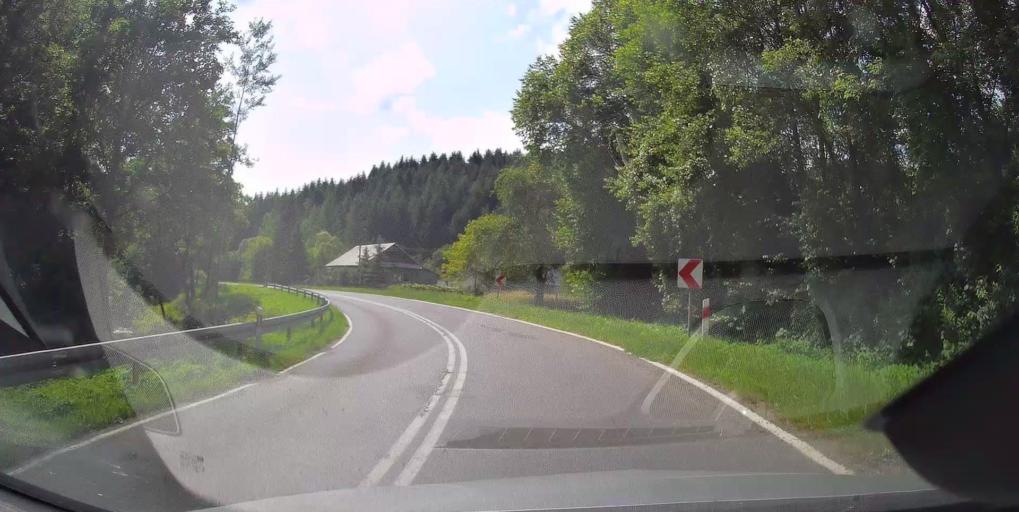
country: PL
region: Lesser Poland Voivodeship
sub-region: Powiat tarnowski
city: Zakliczyn
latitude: 49.8151
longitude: 20.7965
